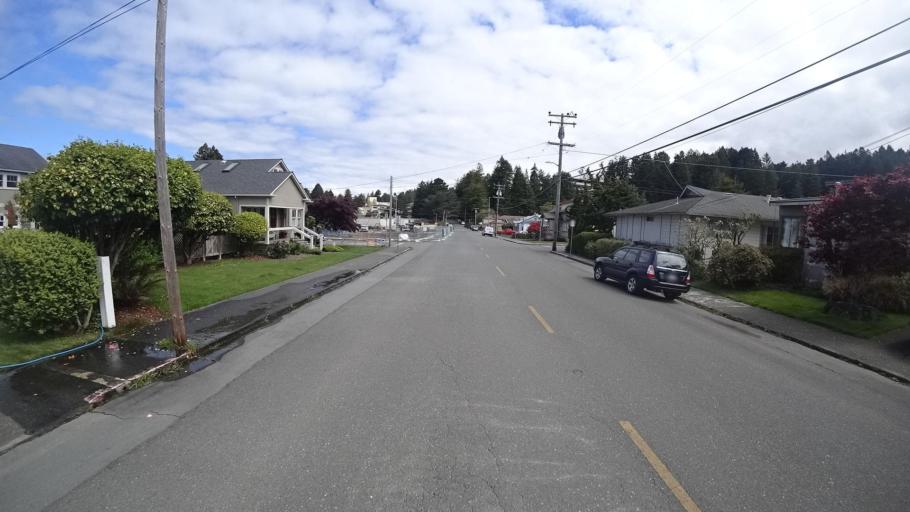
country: US
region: California
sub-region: Humboldt County
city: Arcata
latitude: 40.8706
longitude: -124.0796
